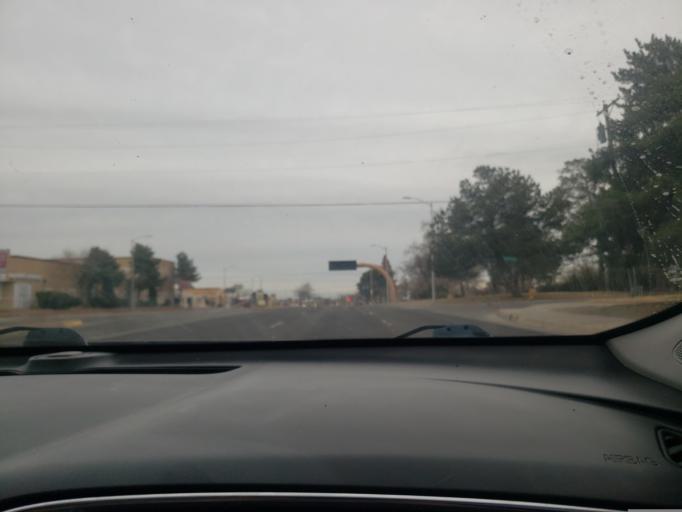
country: US
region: New Mexico
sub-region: Bernalillo County
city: Albuquerque
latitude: 35.0980
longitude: -106.5863
